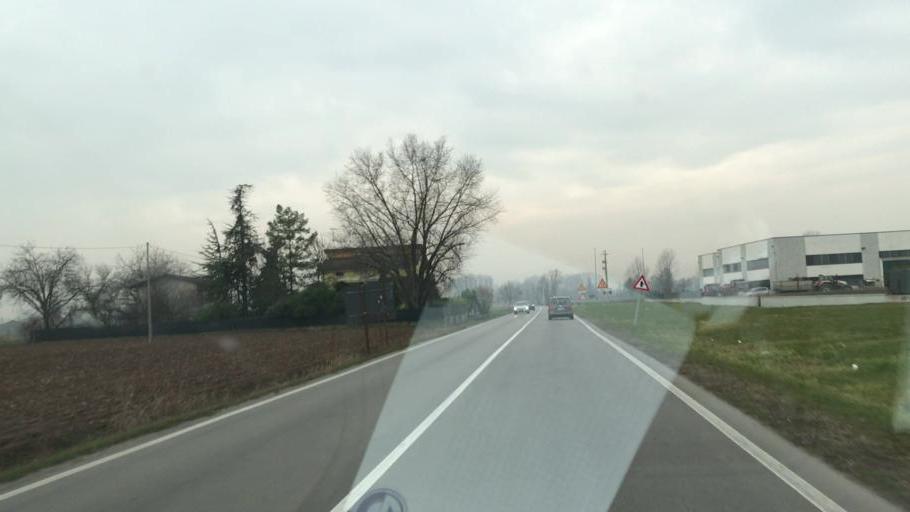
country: IT
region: Lombardy
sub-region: Provincia di Mantova
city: Asola
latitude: 45.2248
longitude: 10.3946
